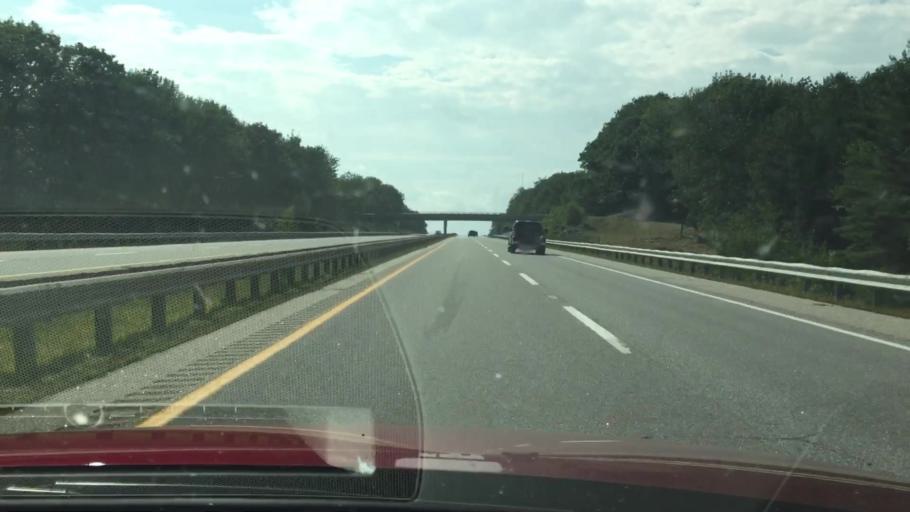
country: US
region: Maine
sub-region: Kennebec County
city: Monmouth
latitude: 44.1253
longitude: -69.9773
